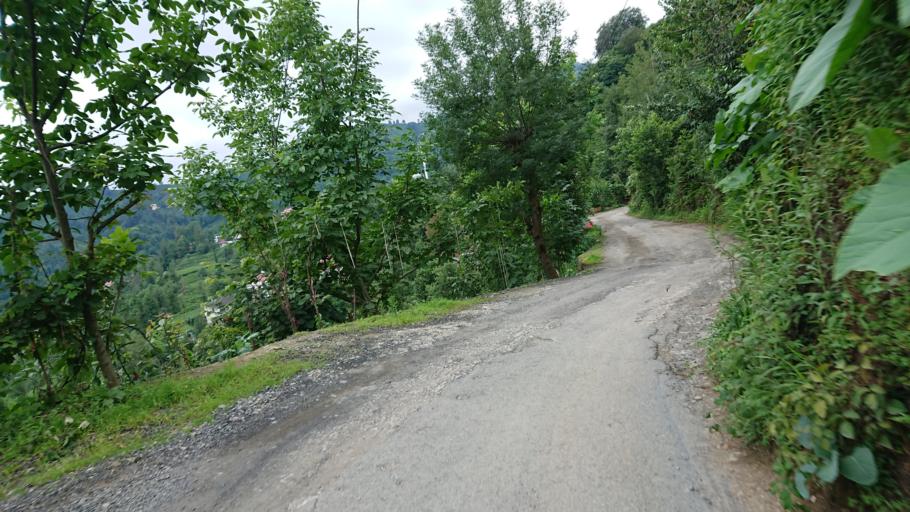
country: TR
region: Rize
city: Rize
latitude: 40.9679
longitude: 40.5128
